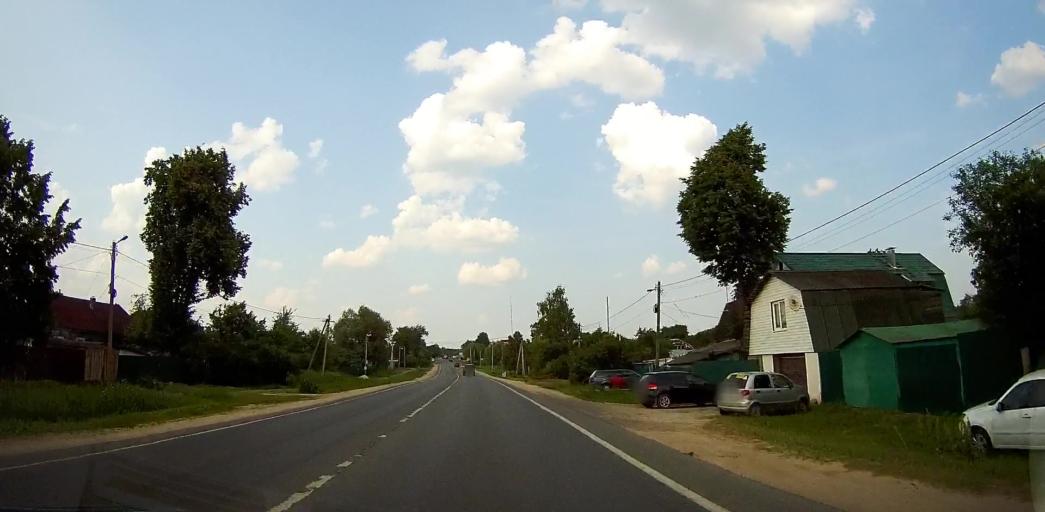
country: RU
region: Moskovskaya
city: Mikhnevo
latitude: 55.1318
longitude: 37.9490
